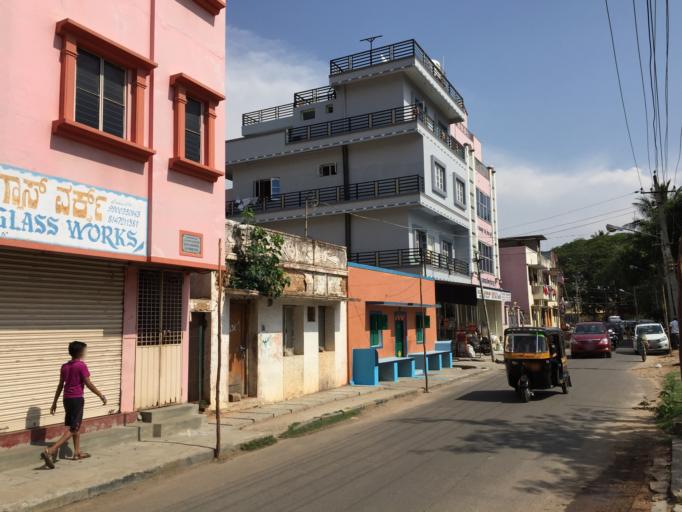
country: IN
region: Karnataka
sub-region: Mysore
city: Mysore
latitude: 12.3051
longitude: 76.6617
